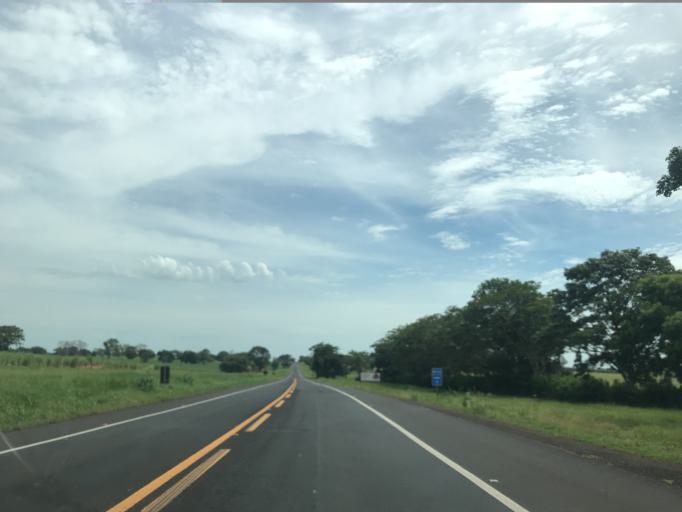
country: BR
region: Sao Paulo
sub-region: Nova Granada
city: Nova Granada
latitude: -20.4057
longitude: -49.2465
